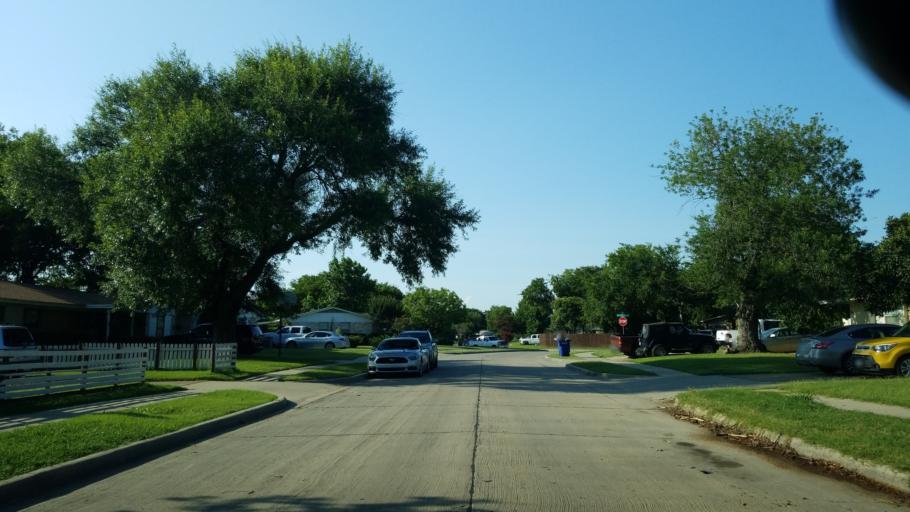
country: US
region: Texas
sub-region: Dallas County
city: Carrollton
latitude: 32.9420
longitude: -96.8985
